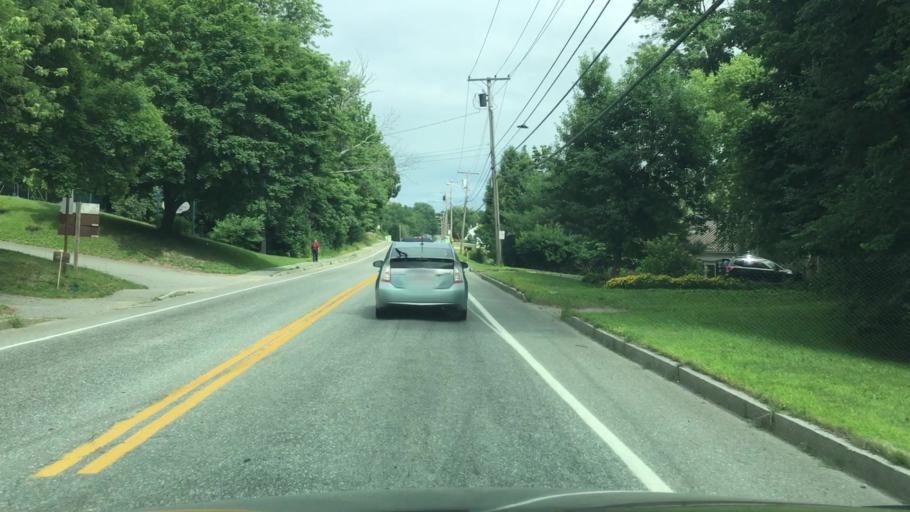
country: US
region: Maine
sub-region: Hancock County
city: Bucksport
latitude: 44.5706
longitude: -68.7815
